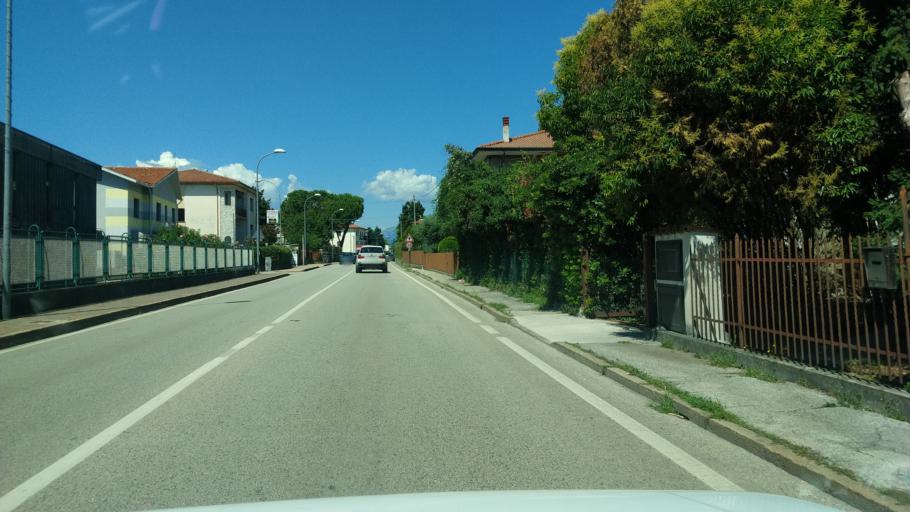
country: IT
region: Veneto
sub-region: Provincia di Vicenza
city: Breganze
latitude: 45.7065
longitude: 11.5637
